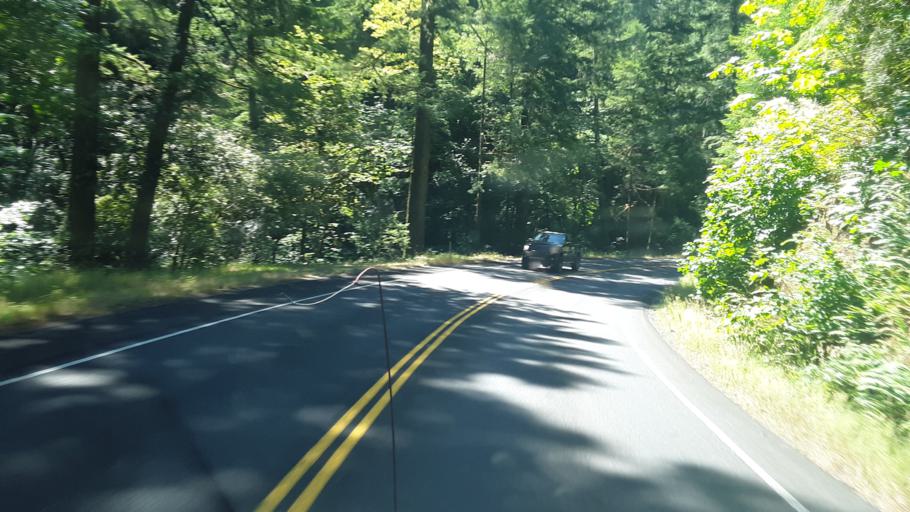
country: US
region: Oregon
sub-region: Josephine County
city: Cave Junction
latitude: 41.9331
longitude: -123.7567
